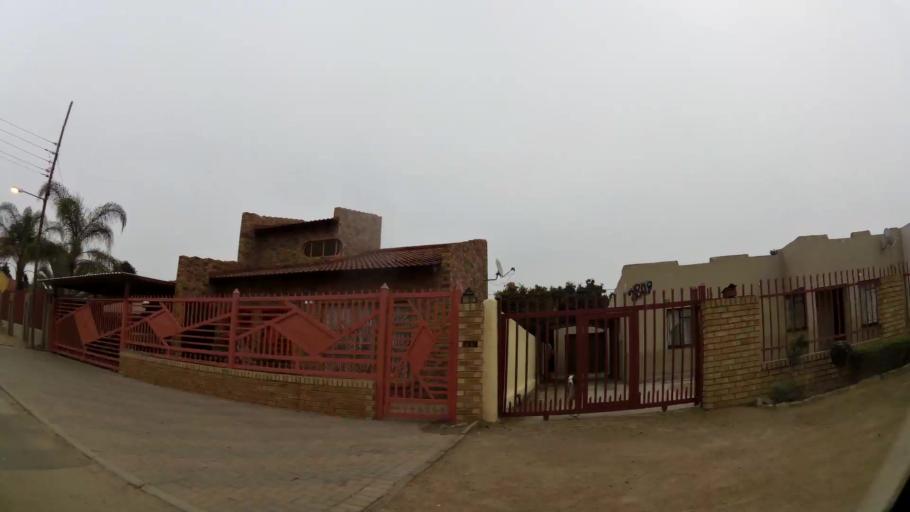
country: ZA
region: Limpopo
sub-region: Capricorn District Municipality
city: Polokwane
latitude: -23.8504
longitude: 29.3947
